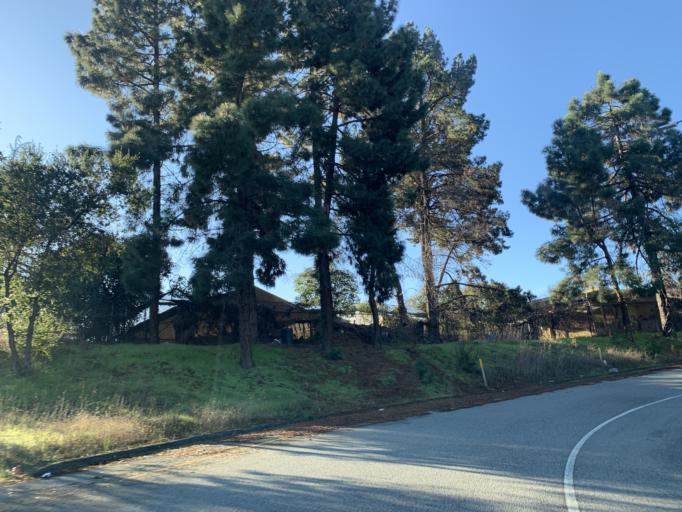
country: US
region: California
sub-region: Santa Clara County
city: Buena Vista
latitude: 37.3122
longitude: -121.9147
